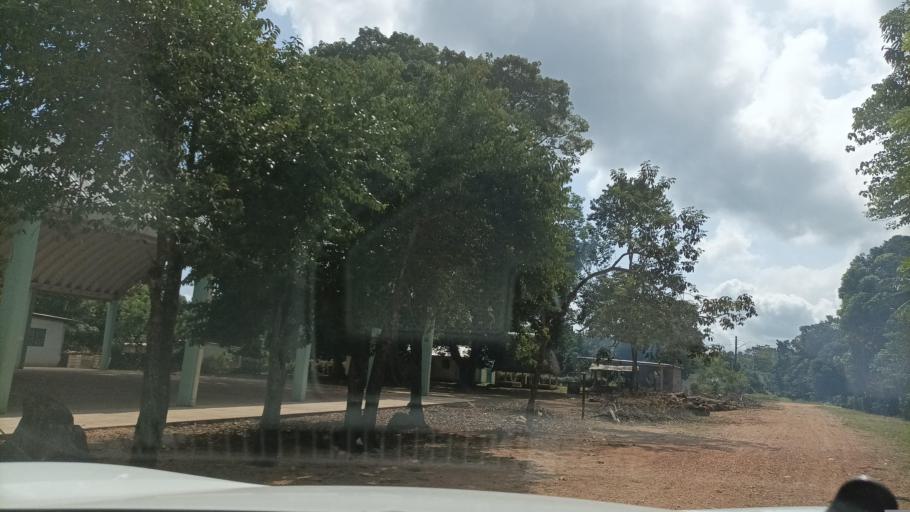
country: MX
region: Veracruz
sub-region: Pajapan
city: Pajapan
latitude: 18.1830
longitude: -94.6720
